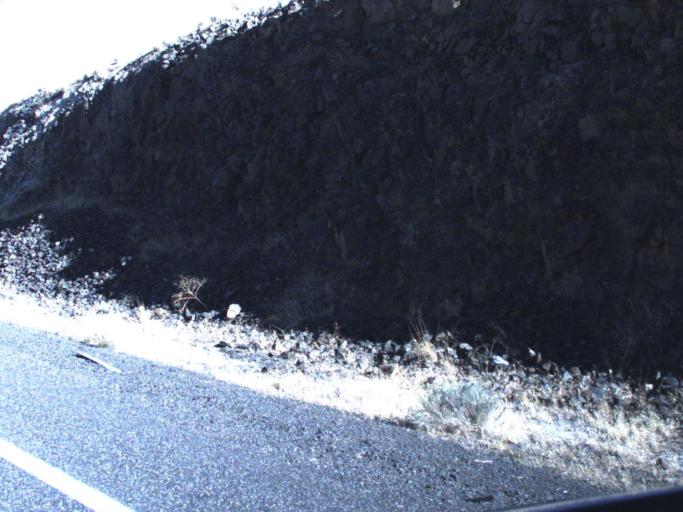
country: US
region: Washington
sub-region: Benton County
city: Highland
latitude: 46.1523
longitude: -119.1764
